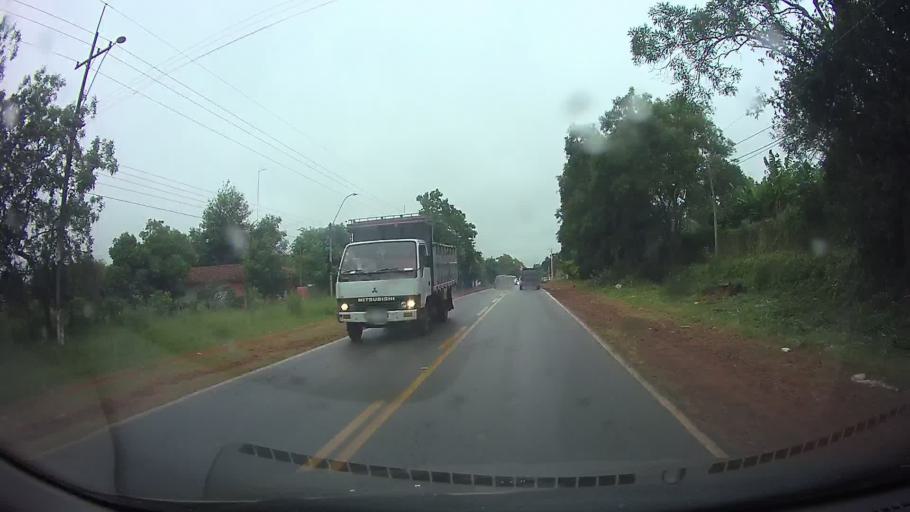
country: PY
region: Central
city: Itaugua
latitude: -25.4267
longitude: -57.3644
